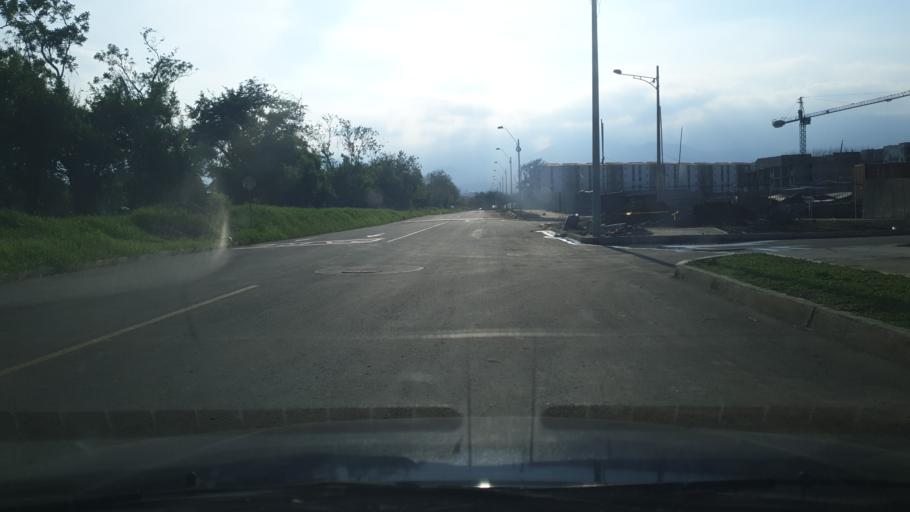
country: CO
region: Valle del Cauca
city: Jamundi
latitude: 3.3444
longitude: -76.5139
